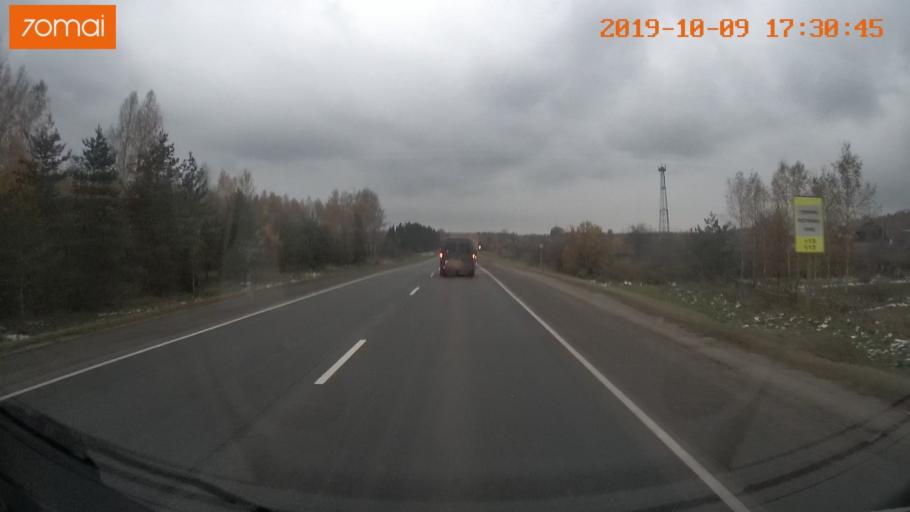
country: RU
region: Ivanovo
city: Bogorodskoye
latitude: 57.1403
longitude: 41.0461
